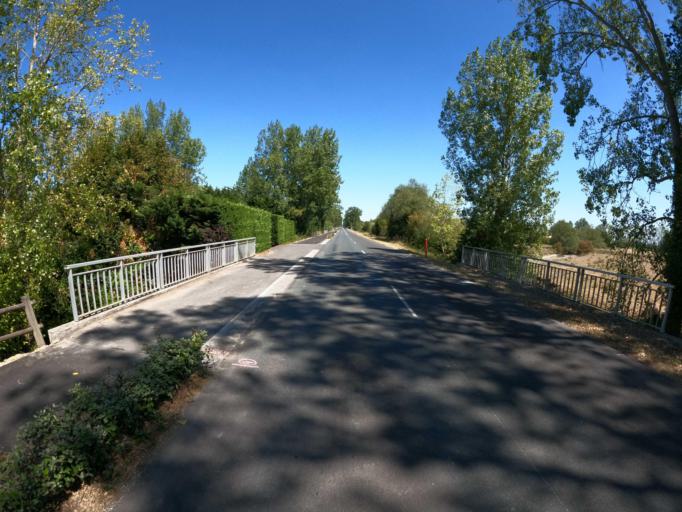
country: FR
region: Pays de la Loire
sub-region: Departement de la Vendee
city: Le Perrier
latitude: 46.8031
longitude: -2.0311
